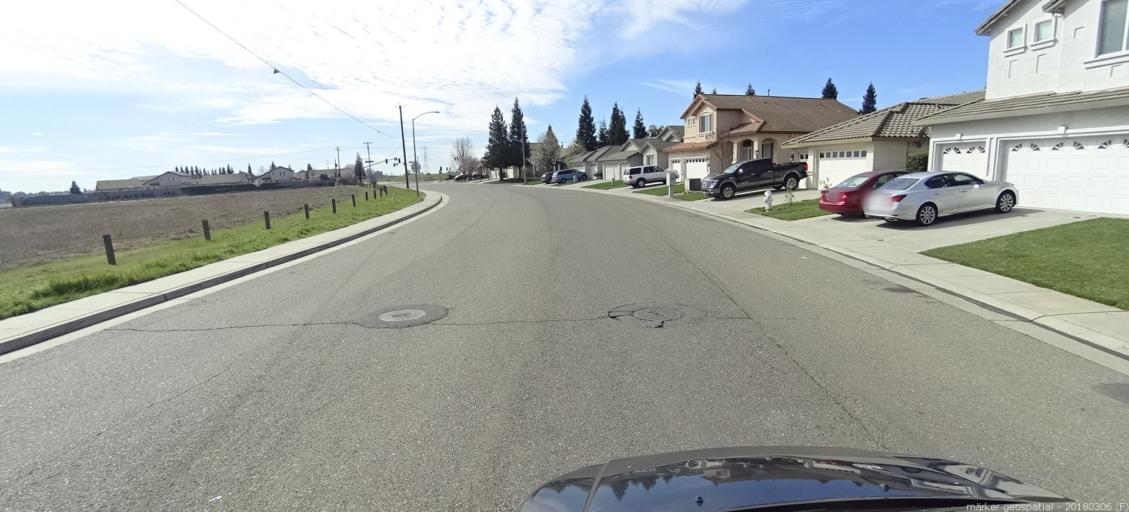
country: US
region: California
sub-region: Sacramento County
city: Vineyard
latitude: 38.4649
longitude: -121.3418
